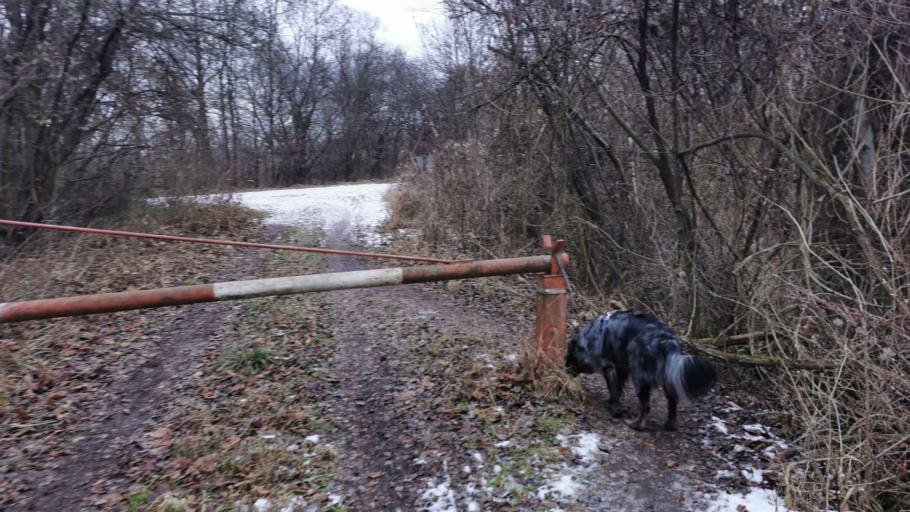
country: DE
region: Bavaria
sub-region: Upper Bavaria
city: Kirchheim bei Muenchen
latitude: 48.1943
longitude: 11.7595
